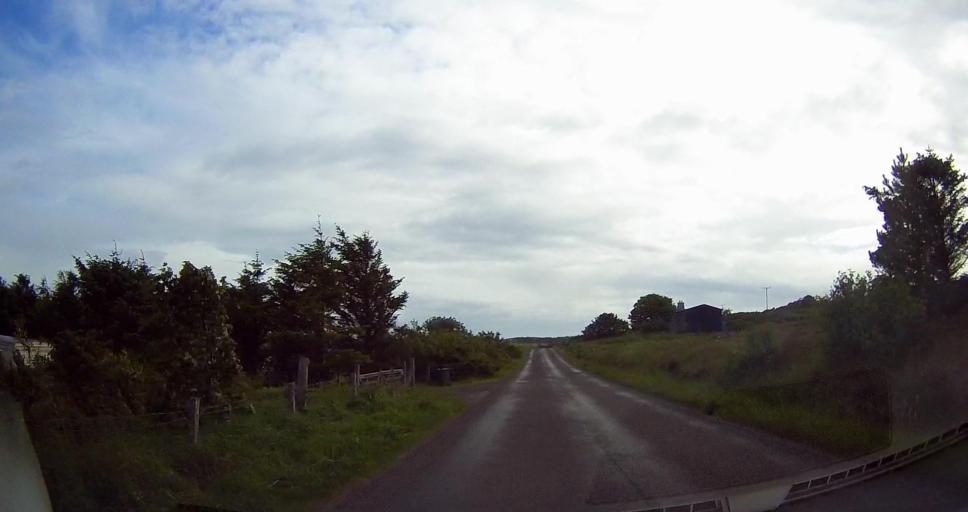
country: GB
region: Scotland
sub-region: Orkney Islands
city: Stromness
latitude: 58.7954
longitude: -3.2536
